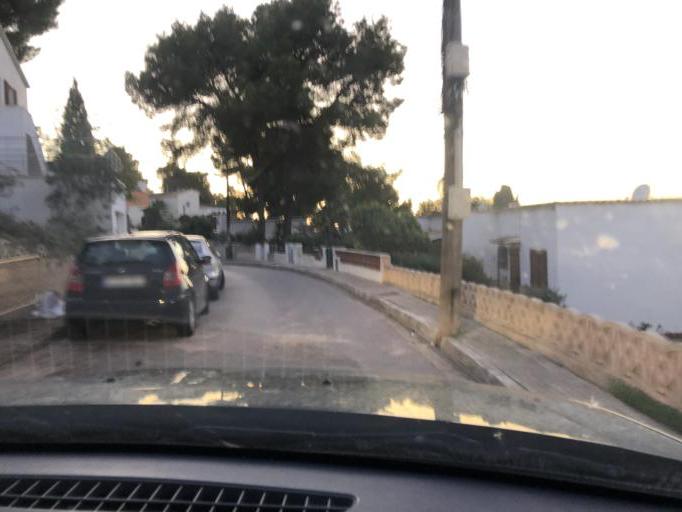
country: ES
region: Balearic Islands
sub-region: Illes Balears
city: Santa Ponsa
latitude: 39.5237
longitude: 2.4790
